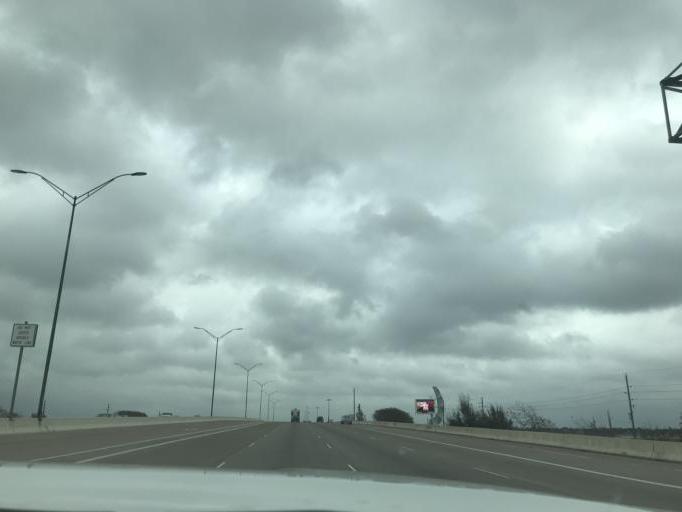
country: US
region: Texas
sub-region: Fort Bend County
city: New Territory
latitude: 29.5794
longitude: -95.6501
